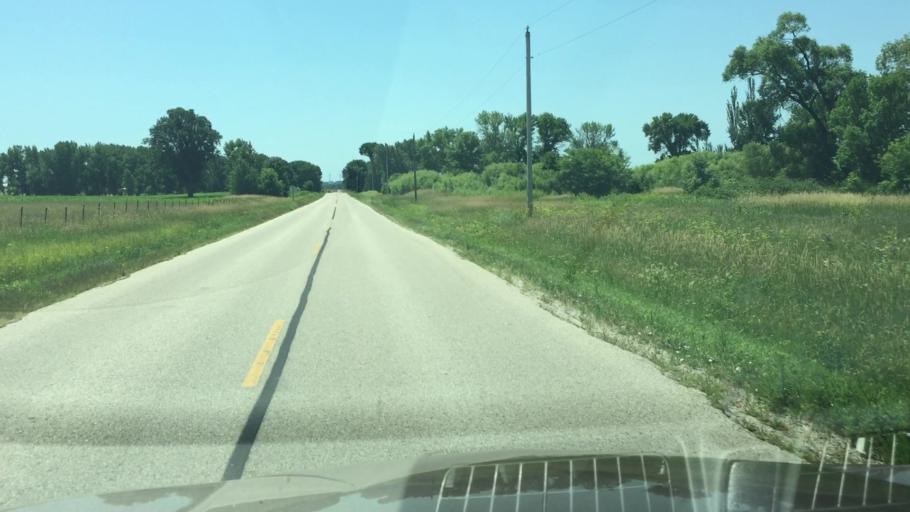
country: US
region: Wisconsin
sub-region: Fond du Lac County
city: Saint Peter
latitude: 43.9662
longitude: -88.3117
